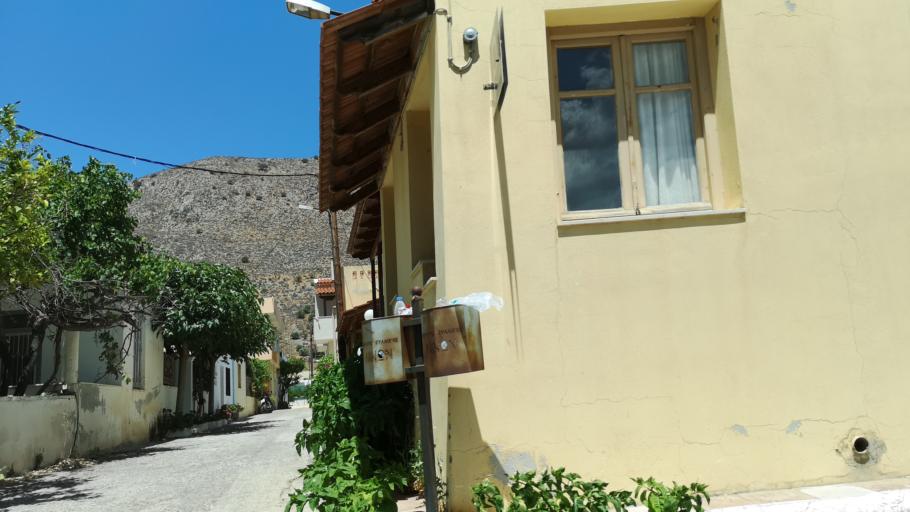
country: GR
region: Crete
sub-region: Nomos Lasithiou
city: Neapoli
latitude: 35.2461
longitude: 25.6387
